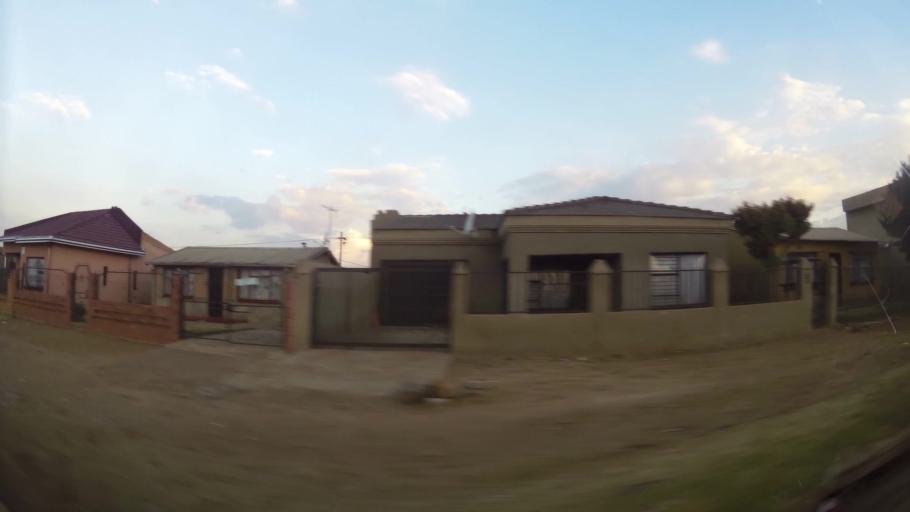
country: ZA
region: Gauteng
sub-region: City of Johannesburg Metropolitan Municipality
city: Orange Farm
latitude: -26.5498
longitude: 27.8690
